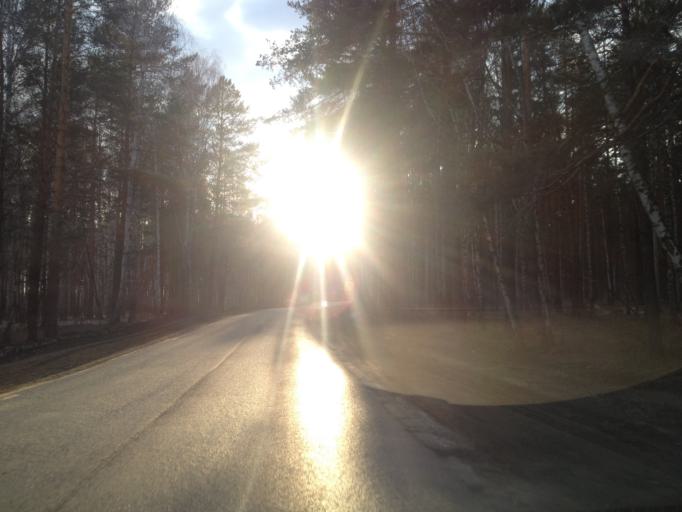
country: RU
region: Sverdlovsk
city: Shirokaya Rechka
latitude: 56.8146
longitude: 60.4396
